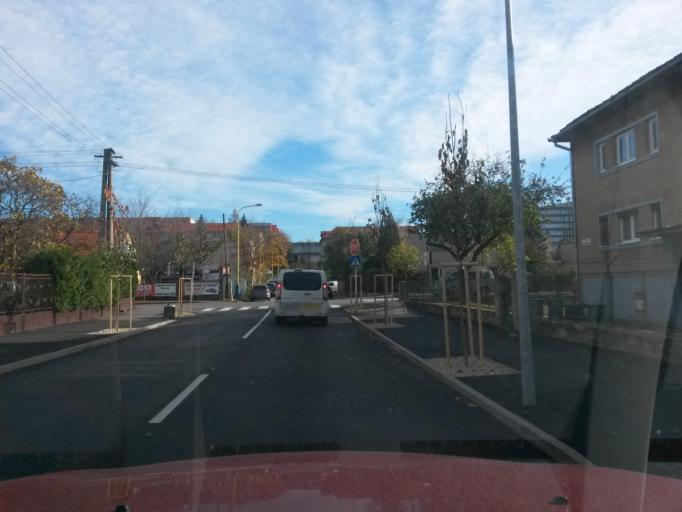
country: SK
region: Presovsky
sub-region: Okres Presov
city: Presov
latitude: 49.0031
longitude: 21.2355
